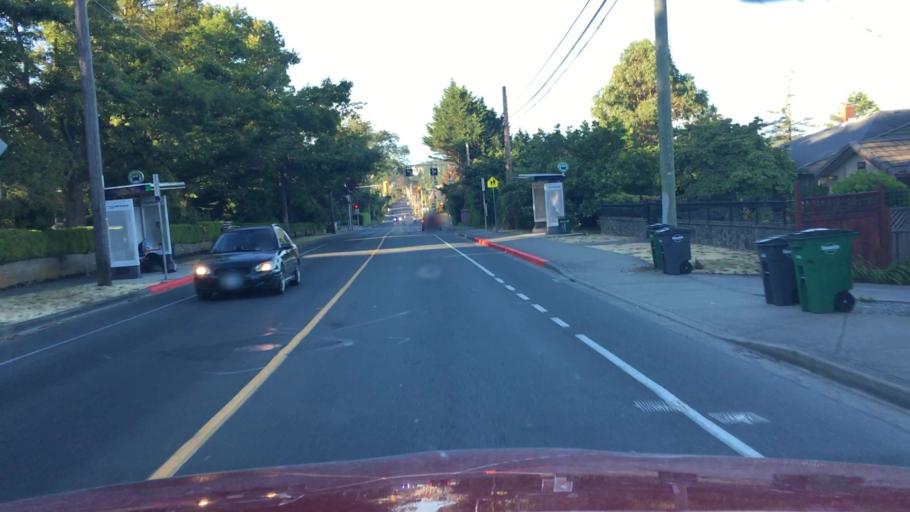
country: CA
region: British Columbia
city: Oak Bay
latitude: 48.4475
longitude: -123.3263
